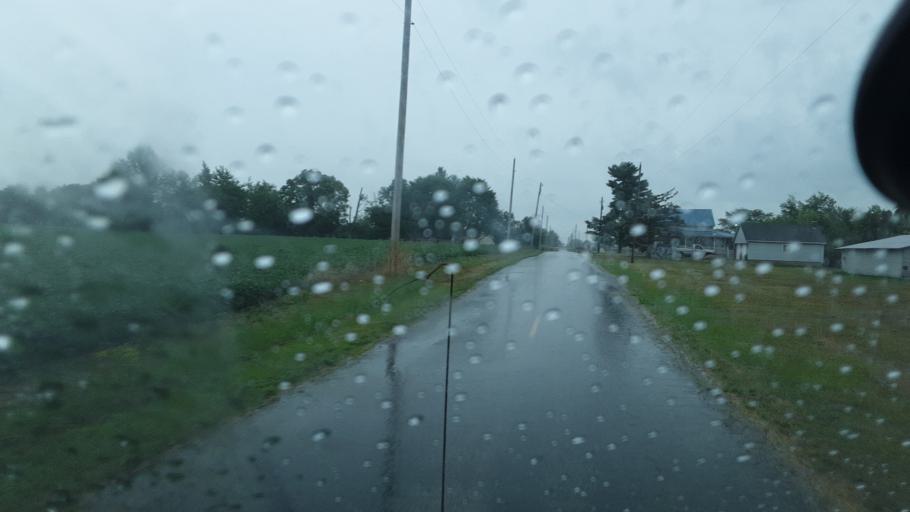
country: US
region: Ohio
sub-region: Williams County
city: Montpelier
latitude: 41.6008
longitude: -84.5629
